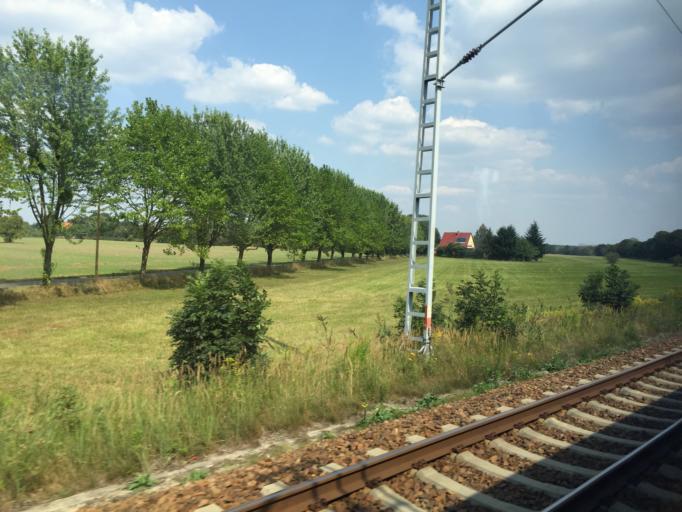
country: DE
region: Brandenburg
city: Welzow
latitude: 51.5763
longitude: 14.0911
